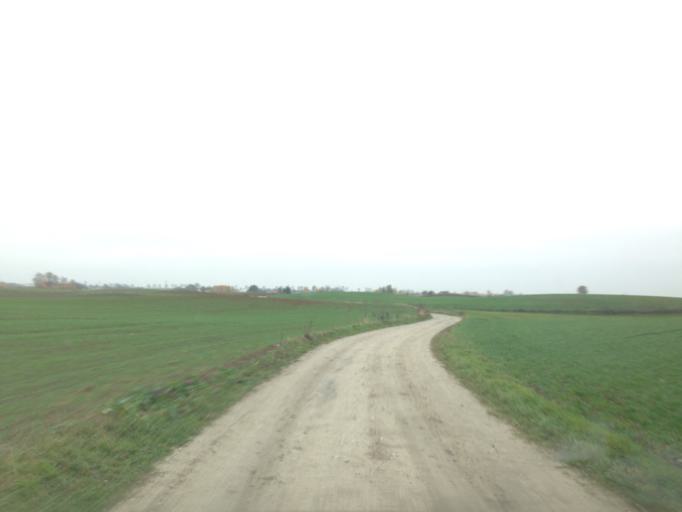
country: PL
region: Kujawsko-Pomorskie
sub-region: Powiat brodnicki
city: Bartniczka
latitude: 53.2205
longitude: 19.6013
